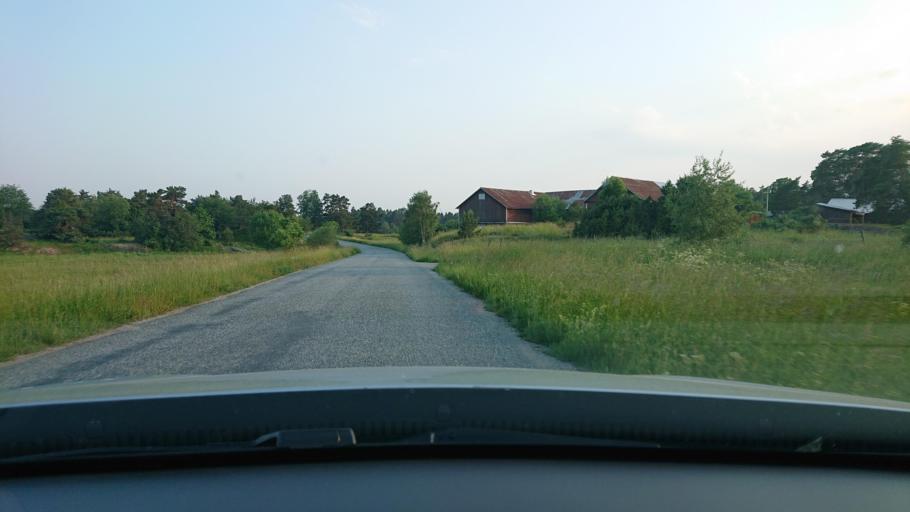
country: SE
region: Stockholm
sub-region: Osterakers Kommun
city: Akersberga
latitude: 59.5101
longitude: 18.3144
